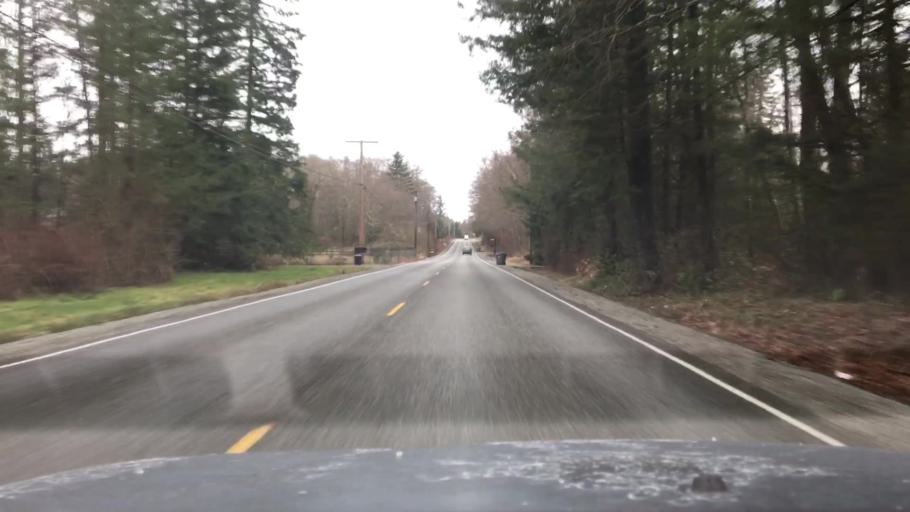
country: US
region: Washington
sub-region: Whatcom County
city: Sudden Valley
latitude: 48.6269
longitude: -122.3211
